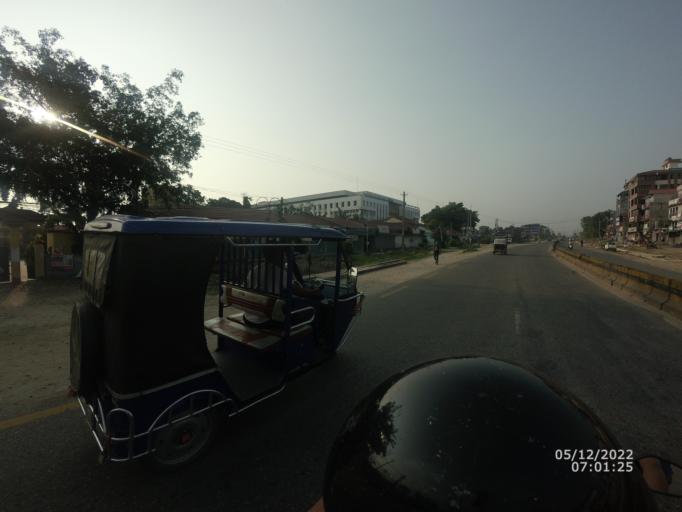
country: NP
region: Central Region
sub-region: Narayani Zone
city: Bharatpur
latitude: 27.6864
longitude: 84.4295
